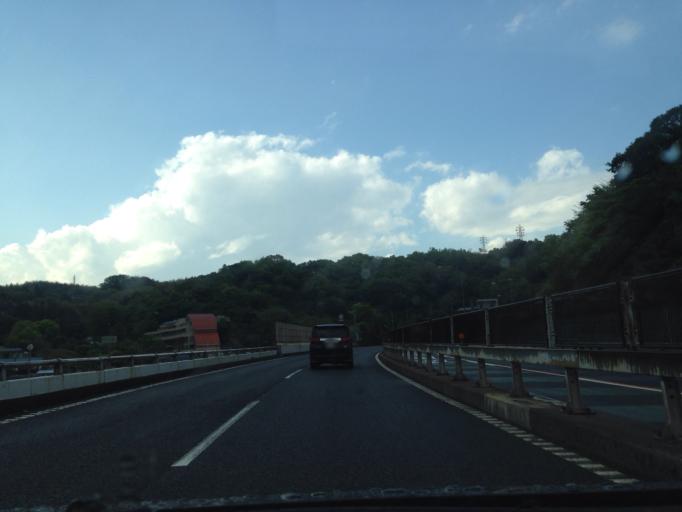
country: JP
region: Kanagawa
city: Odawara
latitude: 35.2463
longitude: 139.1329
